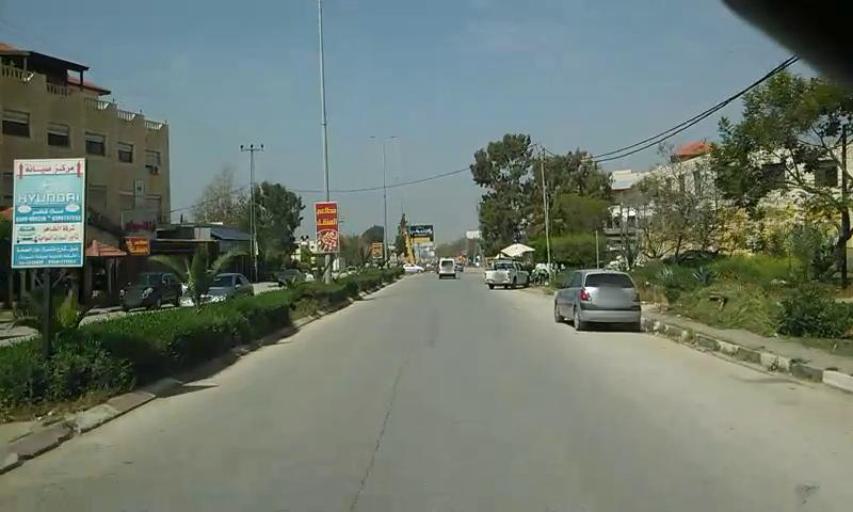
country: PS
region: West Bank
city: Janin
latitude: 32.4694
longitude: 35.3042
